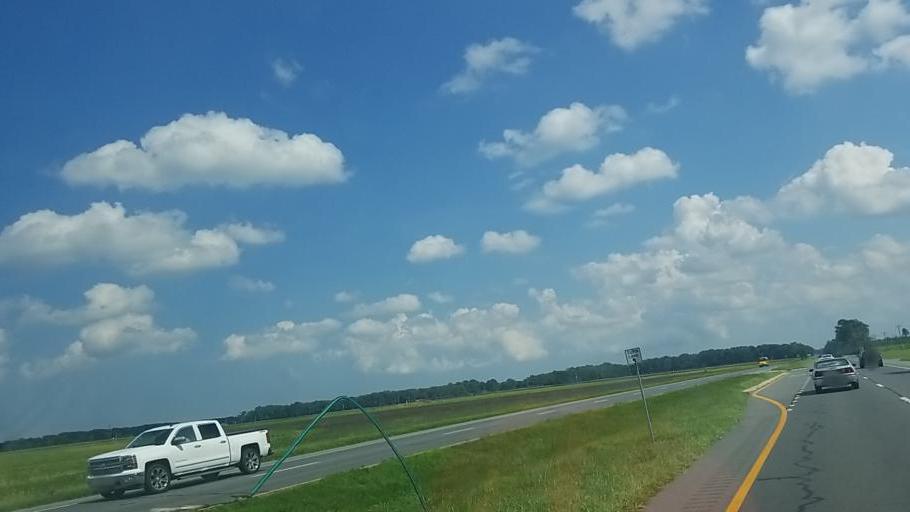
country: US
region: Delaware
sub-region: Sussex County
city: Millsboro
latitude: 38.6236
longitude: -75.3404
